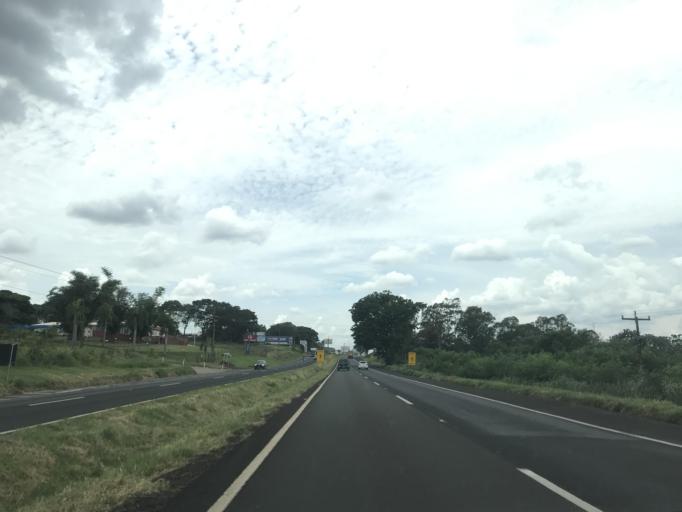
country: BR
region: Parana
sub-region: Paicandu
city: Paicandu
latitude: -23.3894
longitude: -52.0167
